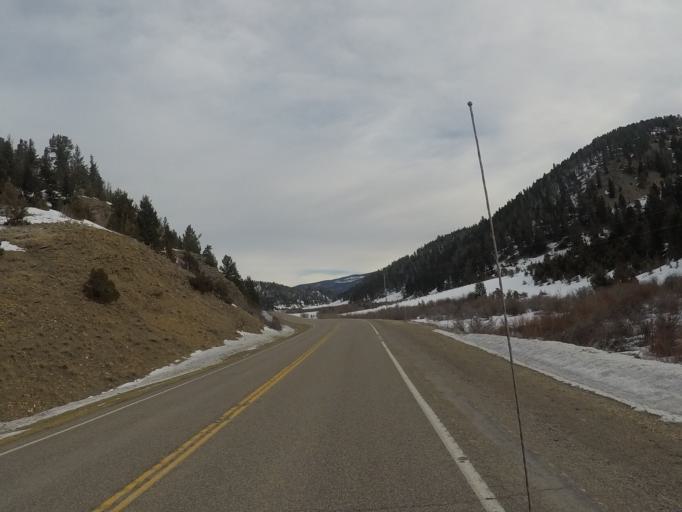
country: US
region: Montana
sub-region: Meagher County
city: White Sulphur Springs
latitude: 46.6796
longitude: -110.8768
